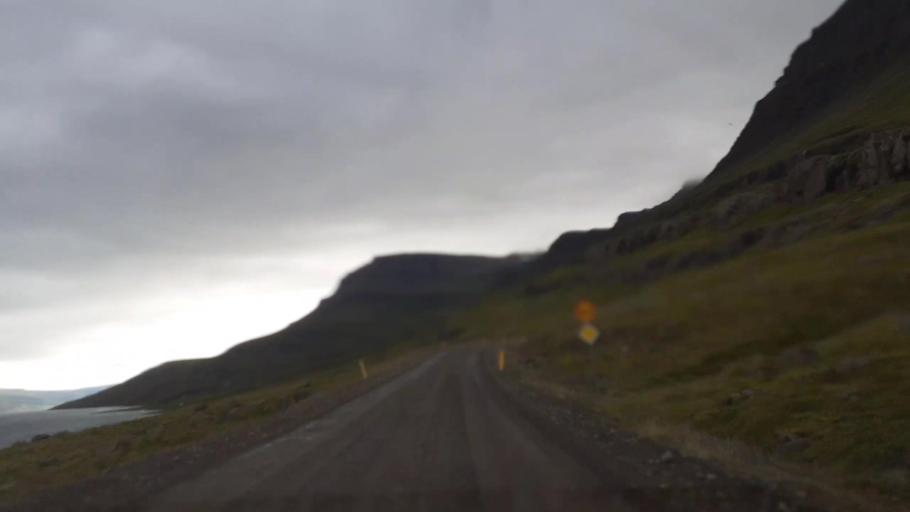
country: IS
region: East
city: Reydarfjoerdur
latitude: 65.0138
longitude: -14.1881
